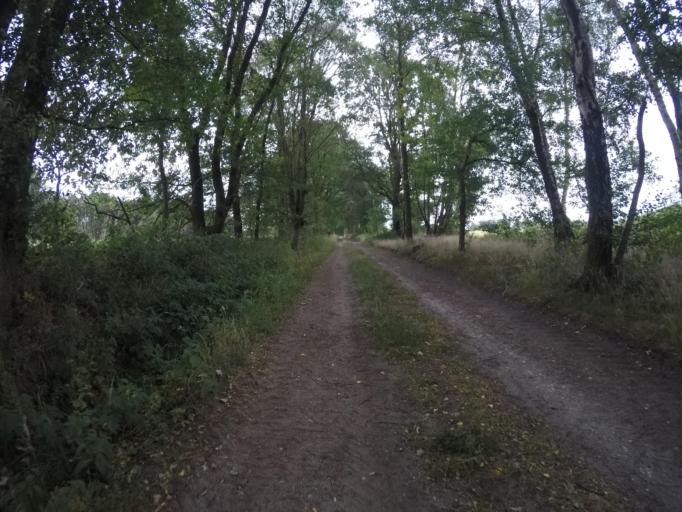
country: DE
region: North Rhine-Westphalia
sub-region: Regierungsbezirk Dusseldorf
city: Bocholt
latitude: 51.8051
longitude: 6.6209
